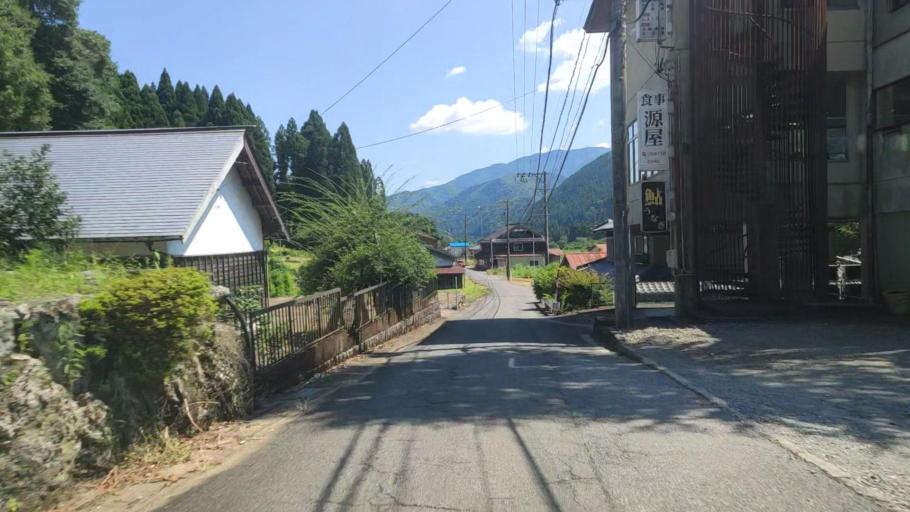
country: JP
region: Gifu
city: Godo
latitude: 35.6799
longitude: 136.5716
